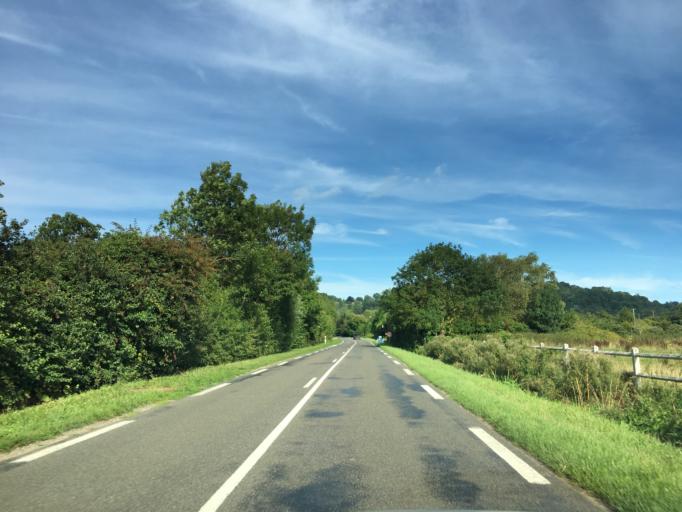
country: FR
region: Lower Normandy
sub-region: Departement du Calvados
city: Cambremer
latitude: 49.1409
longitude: 0.0044
